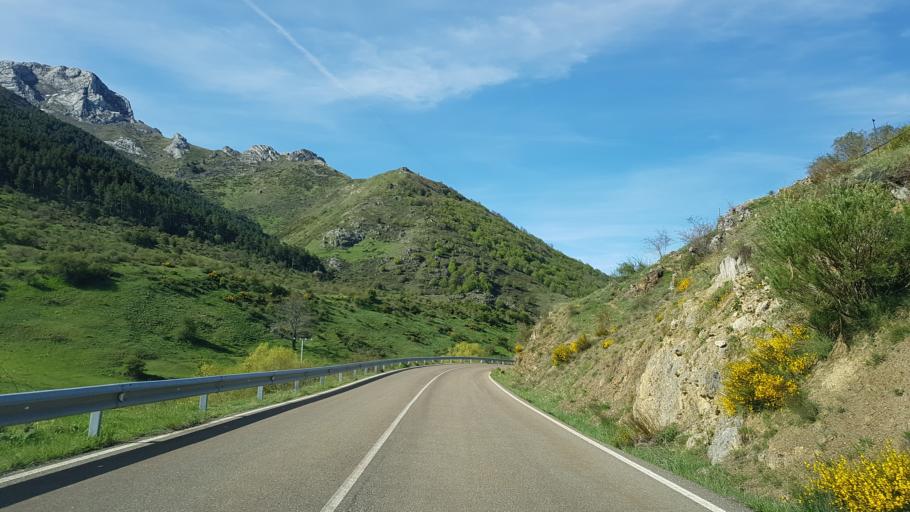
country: ES
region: Castille and Leon
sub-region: Provincia de Leon
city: Villamanin
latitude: 42.9555
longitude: -5.6197
